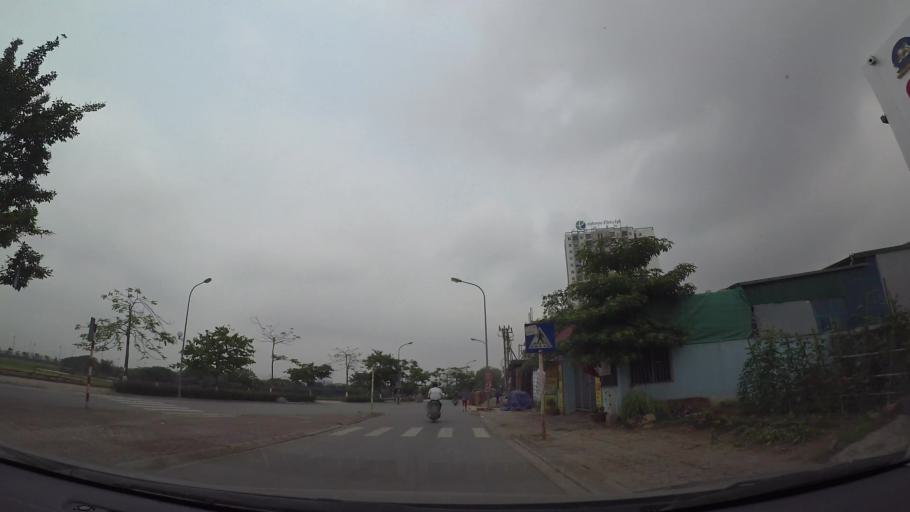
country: VN
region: Ha Noi
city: Trau Quy
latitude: 21.0392
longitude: 105.9293
